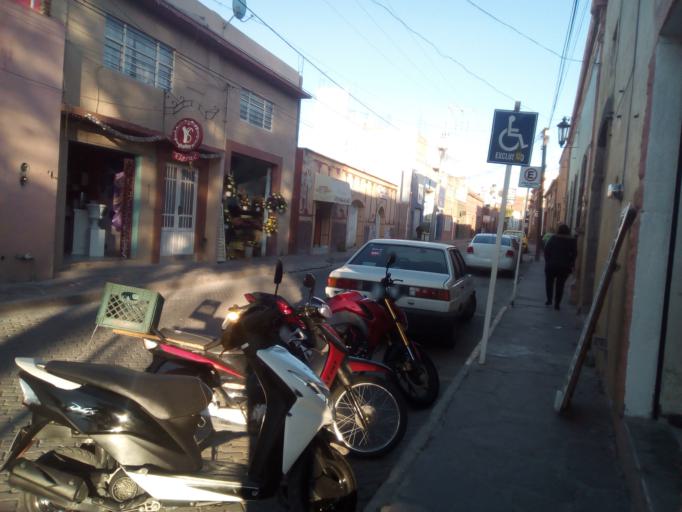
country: MX
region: Guerrero
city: San Luis de la Paz
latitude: 21.2974
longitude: -100.5168
